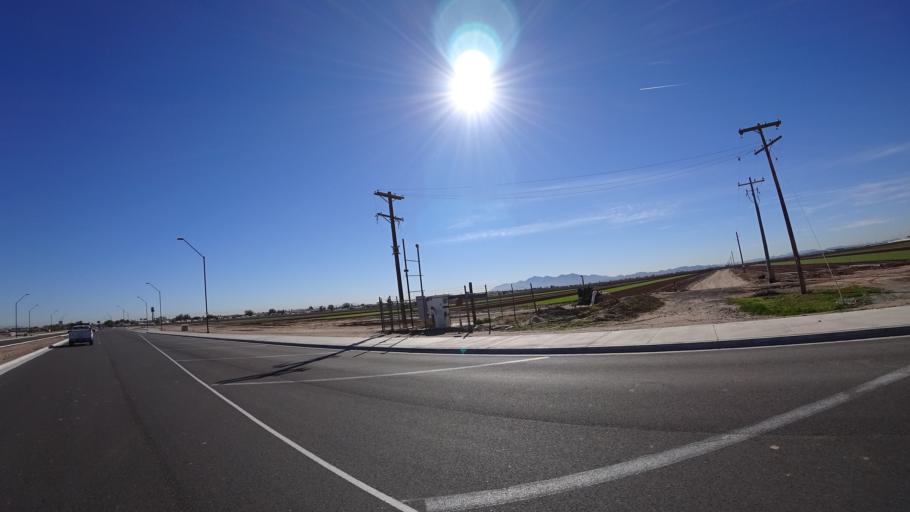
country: US
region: Arizona
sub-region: Maricopa County
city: Litchfield Park
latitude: 33.4936
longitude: -112.4184
